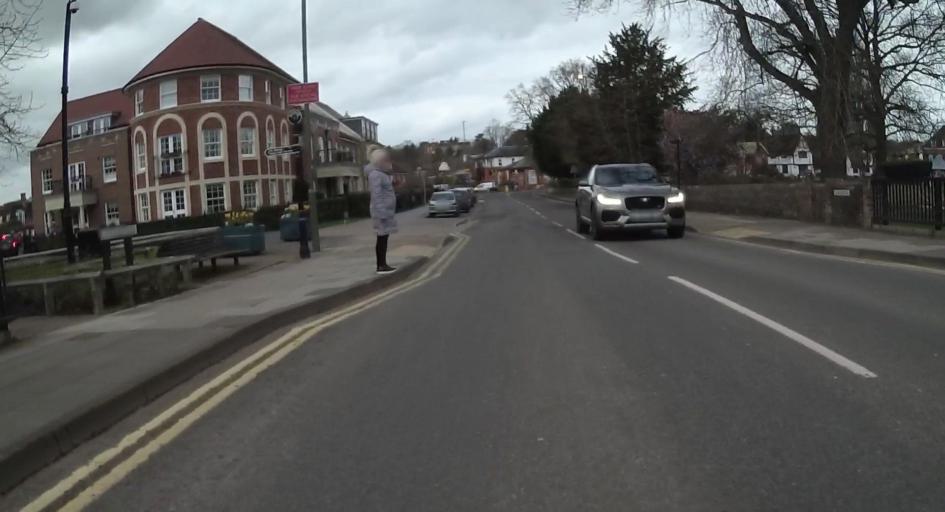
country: GB
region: England
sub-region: Surrey
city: Farnham
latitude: 51.2122
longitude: -0.7971
